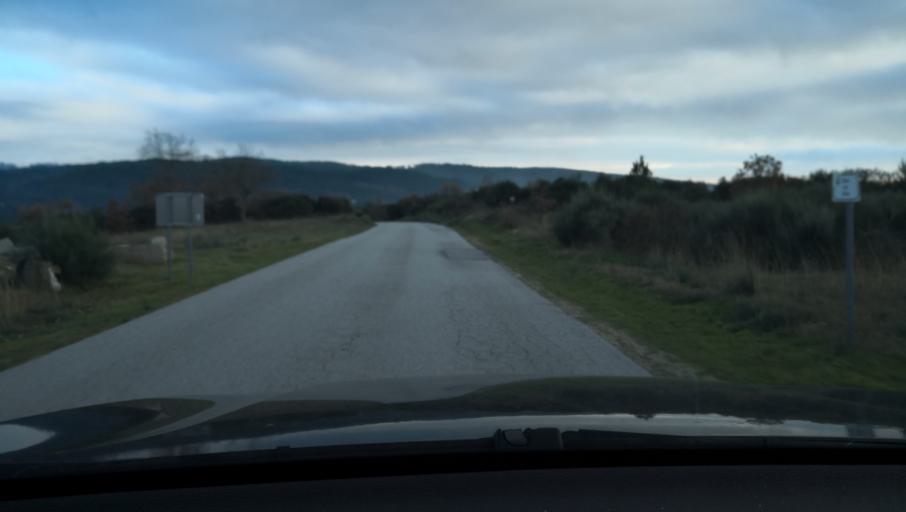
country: PT
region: Vila Real
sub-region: Vila Real
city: Vila Real
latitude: 41.3492
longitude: -7.6645
